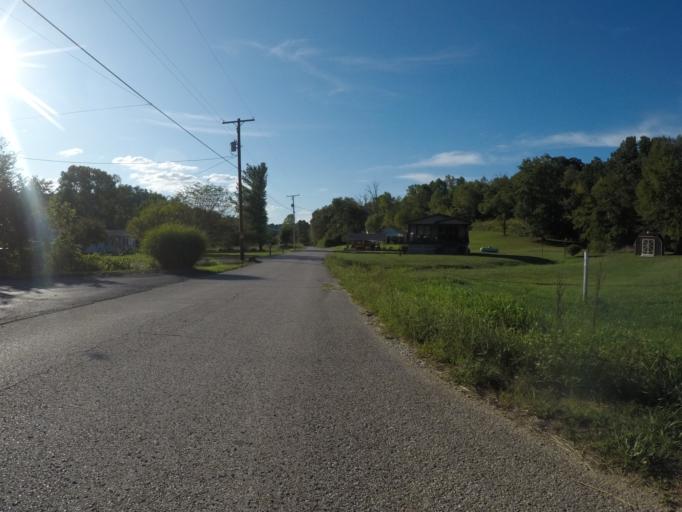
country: US
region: West Virginia
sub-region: Cabell County
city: Huntington
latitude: 38.5085
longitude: -82.4925
